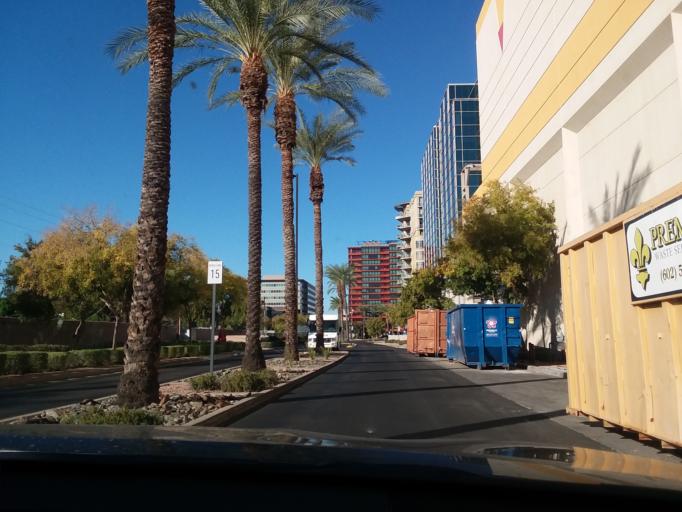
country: US
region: Arizona
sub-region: Maricopa County
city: Phoenix
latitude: 33.5078
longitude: -112.0276
